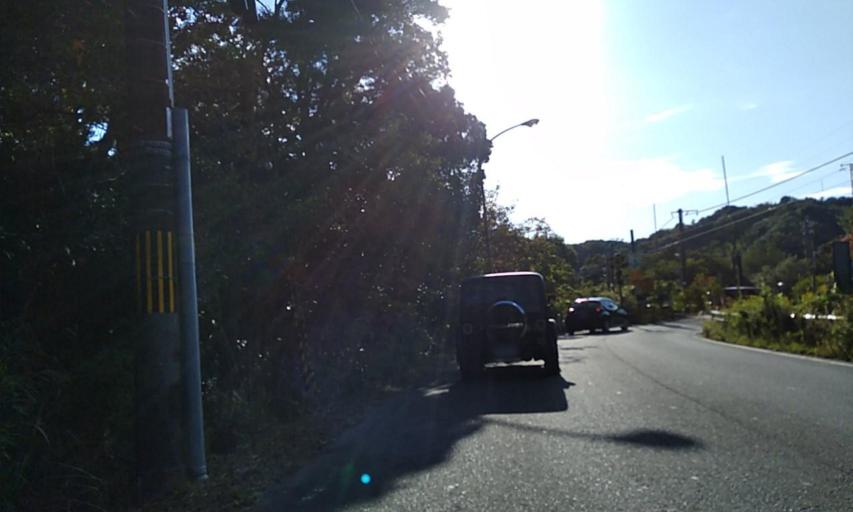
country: JP
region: Wakayama
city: Tanabe
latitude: 33.6820
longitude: 135.3981
